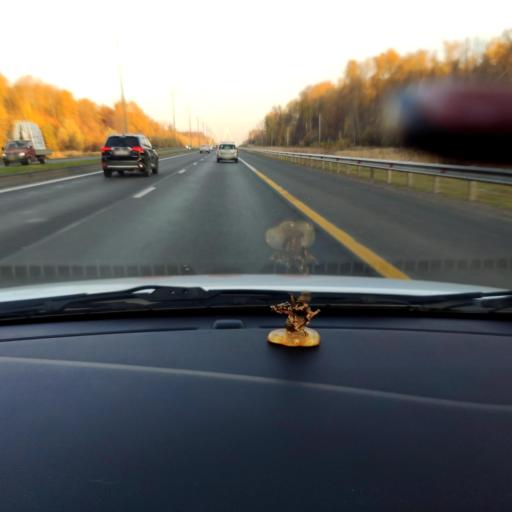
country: RU
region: Tatarstan
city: Stolbishchi
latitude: 55.7055
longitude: 49.2208
